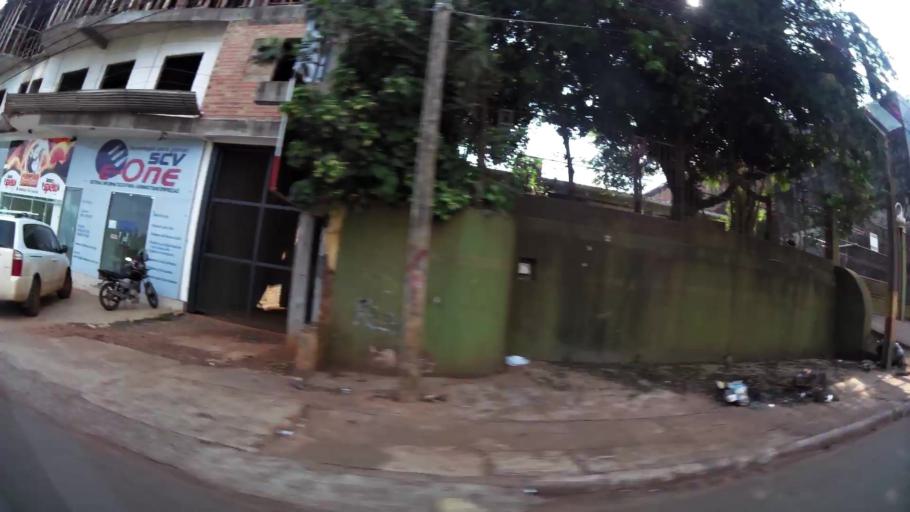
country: PY
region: Alto Parana
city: Presidente Franco
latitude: -25.5247
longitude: -54.6381
